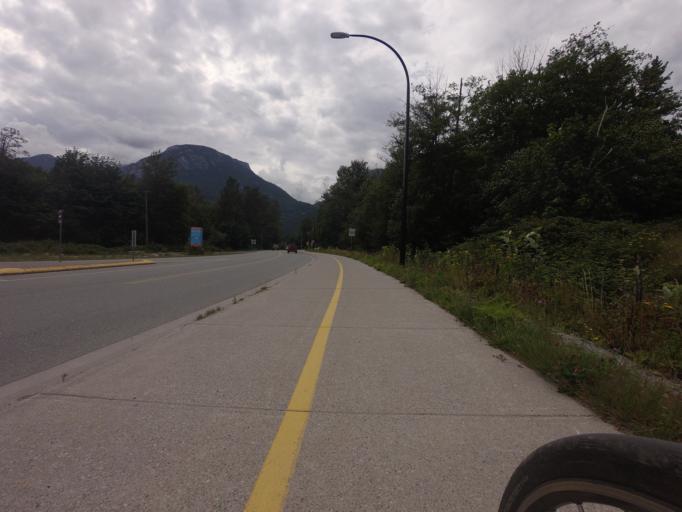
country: CA
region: British Columbia
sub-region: Greater Vancouver Regional District
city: Lions Bay
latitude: 49.7294
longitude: -123.1441
